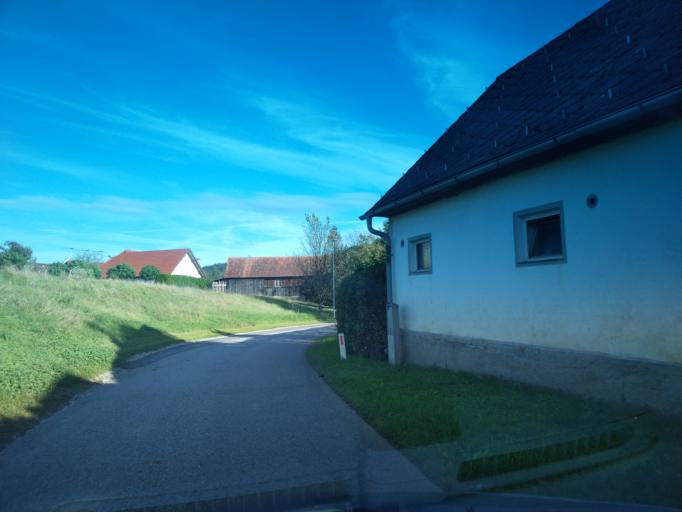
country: AT
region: Styria
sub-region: Politischer Bezirk Deutschlandsberg
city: Sankt Martin im Sulmtal
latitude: 46.7325
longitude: 15.3090
